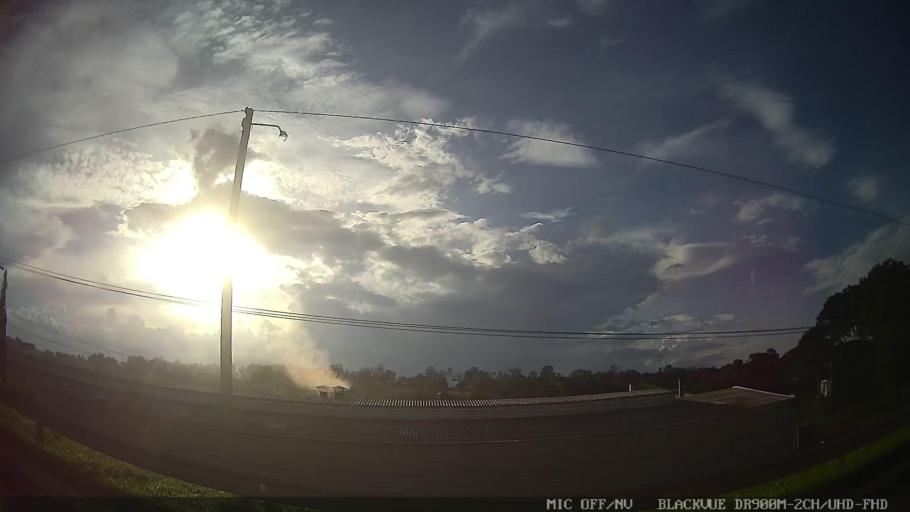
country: BR
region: Sao Paulo
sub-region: Tiete
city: Tiete
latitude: -23.0959
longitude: -47.7233
